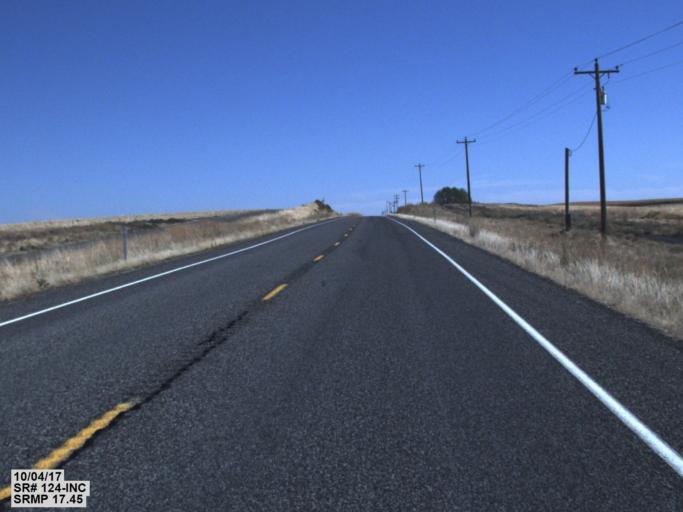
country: US
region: Washington
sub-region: Walla Walla County
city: Burbank
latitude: 46.2974
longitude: -118.6915
